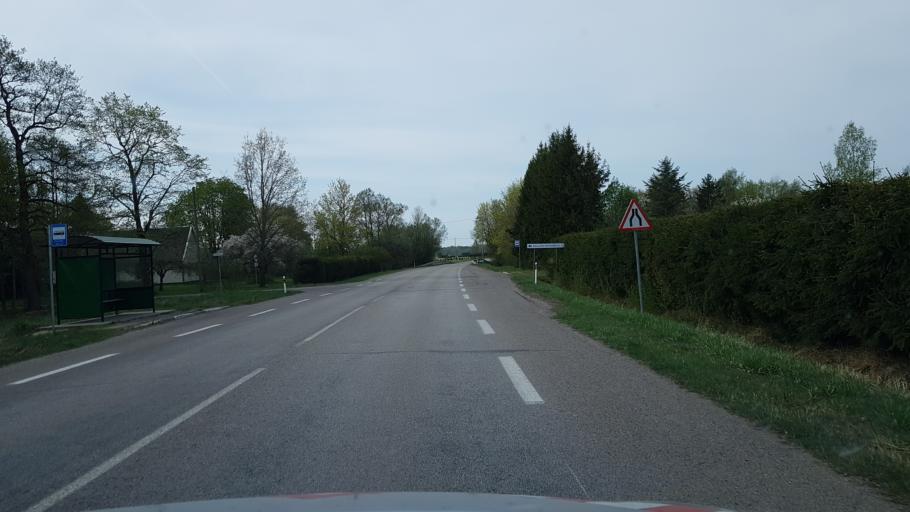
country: EE
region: Paernumaa
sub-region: Audru vald
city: Audru
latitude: 58.3710
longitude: 24.2691
